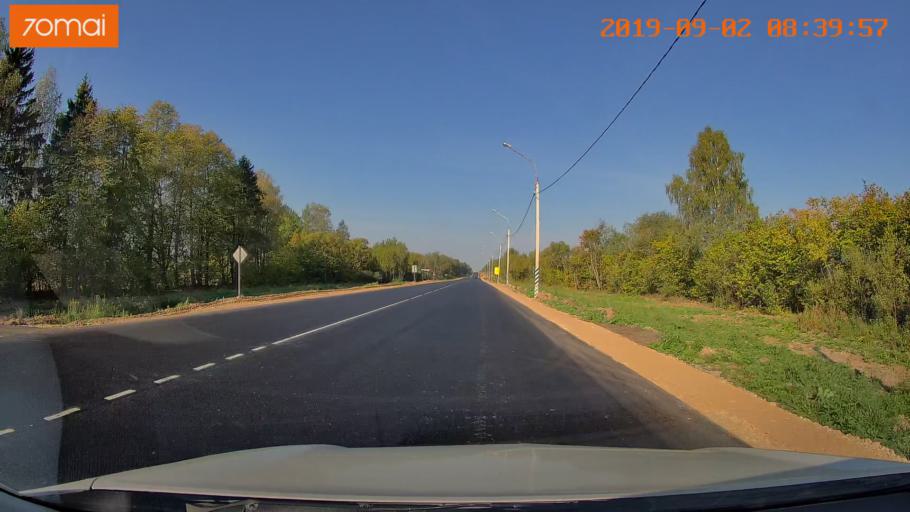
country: RU
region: Kaluga
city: Kudinovo
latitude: 54.9745
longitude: 36.1479
